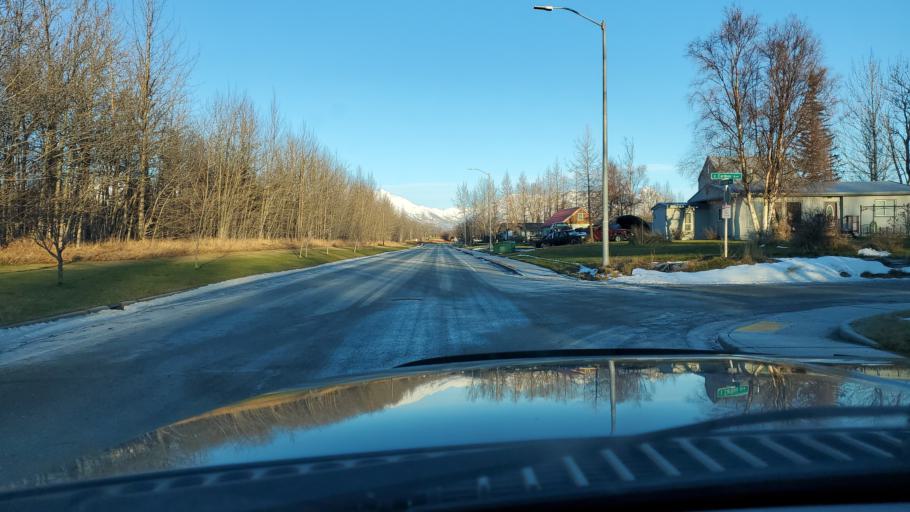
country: US
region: Alaska
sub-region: Matanuska-Susitna Borough
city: Palmer
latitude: 61.6108
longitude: -149.1082
